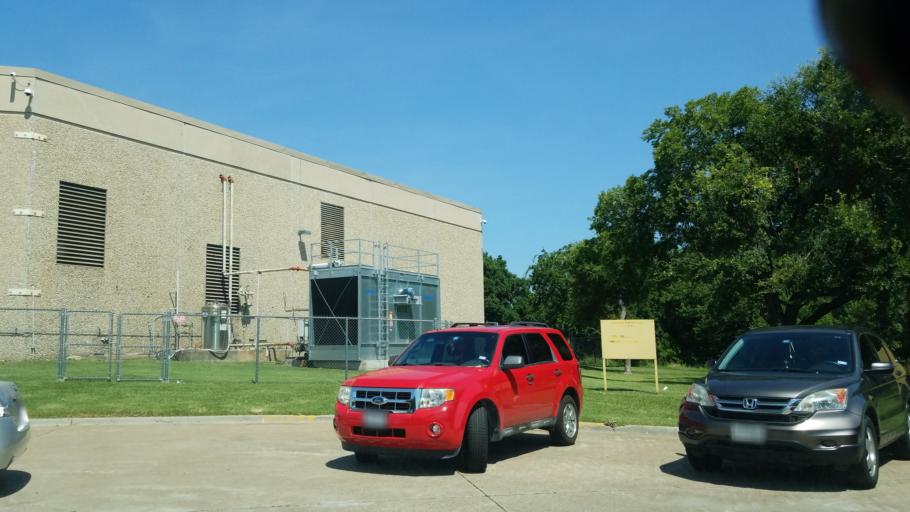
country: US
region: Texas
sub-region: Dallas County
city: Farmers Branch
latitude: 32.9160
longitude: -96.9054
